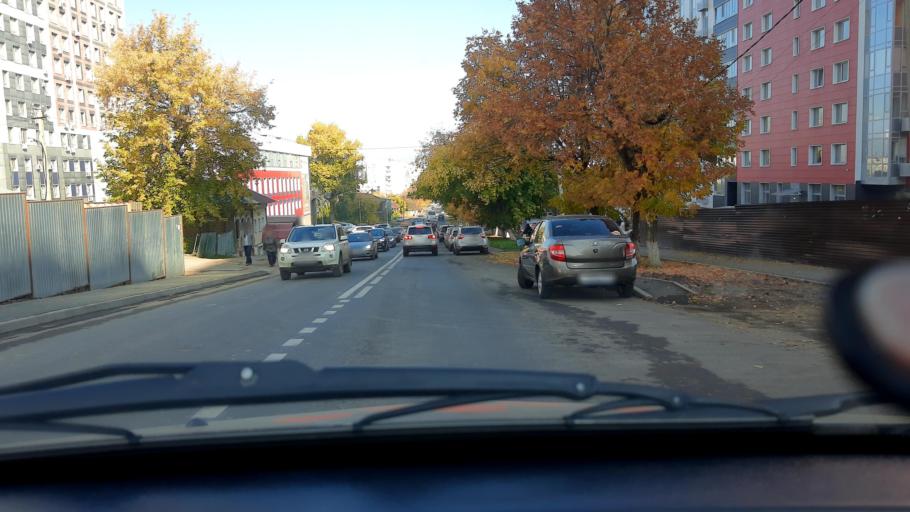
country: RU
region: Bashkortostan
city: Ufa
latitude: 54.7303
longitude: 55.9302
